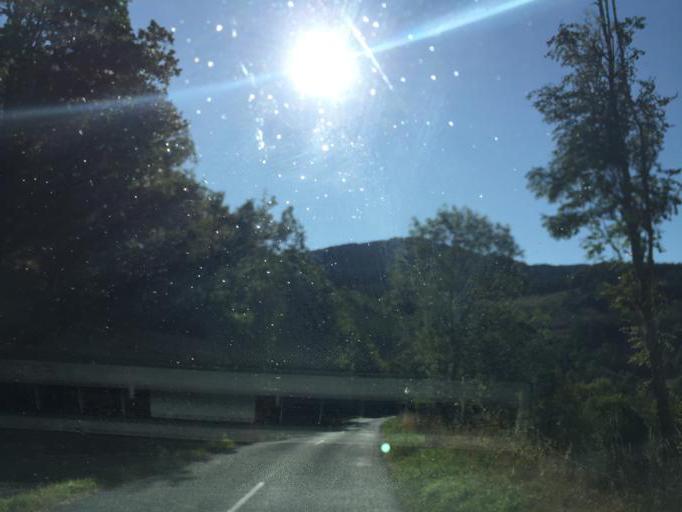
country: FR
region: Rhone-Alpes
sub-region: Departement de la Loire
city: Saint-Chamond
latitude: 45.4113
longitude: 4.5506
